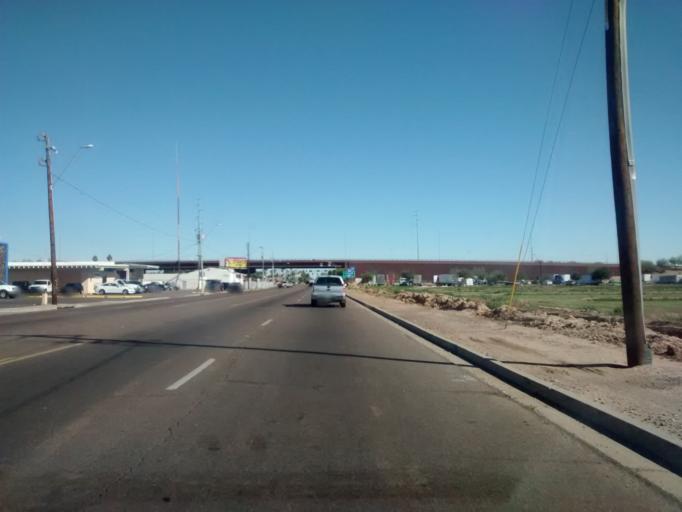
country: US
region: Arizona
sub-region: Maricopa County
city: Glendale
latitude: 33.5239
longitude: -112.1726
